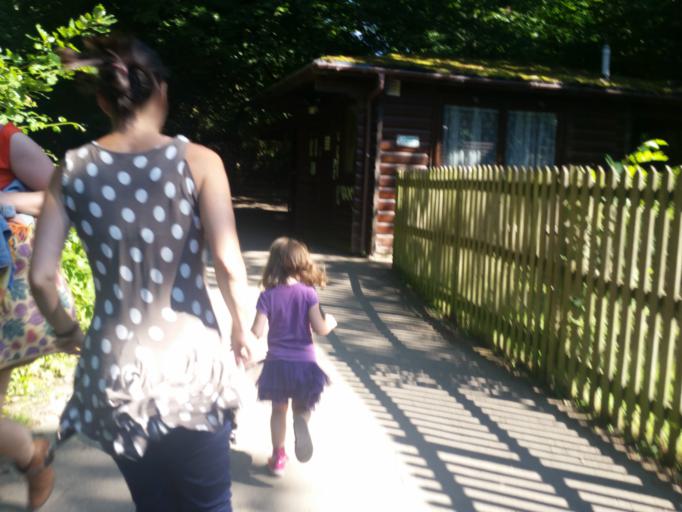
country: GB
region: England
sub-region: Greater London
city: Crouch End
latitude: 51.5799
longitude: -0.1501
